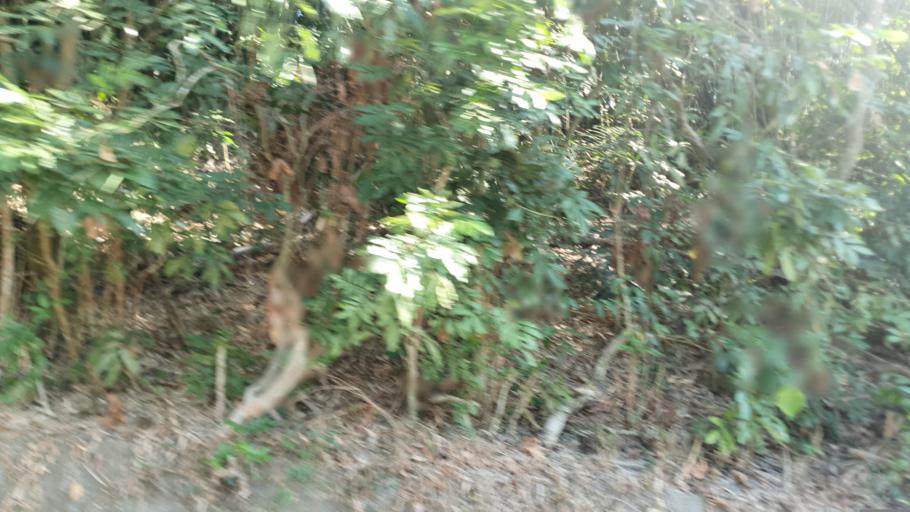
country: TW
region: Taiwan
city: Yujing
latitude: 23.0255
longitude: 120.3894
